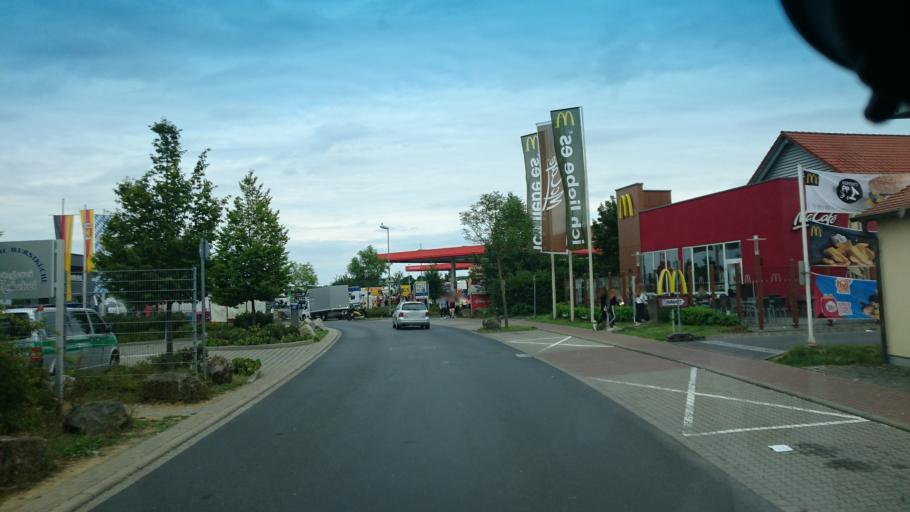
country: DE
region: Bavaria
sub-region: Regierungsbezirk Unterfranken
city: Werneck
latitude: 50.0036
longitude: 10.1168
